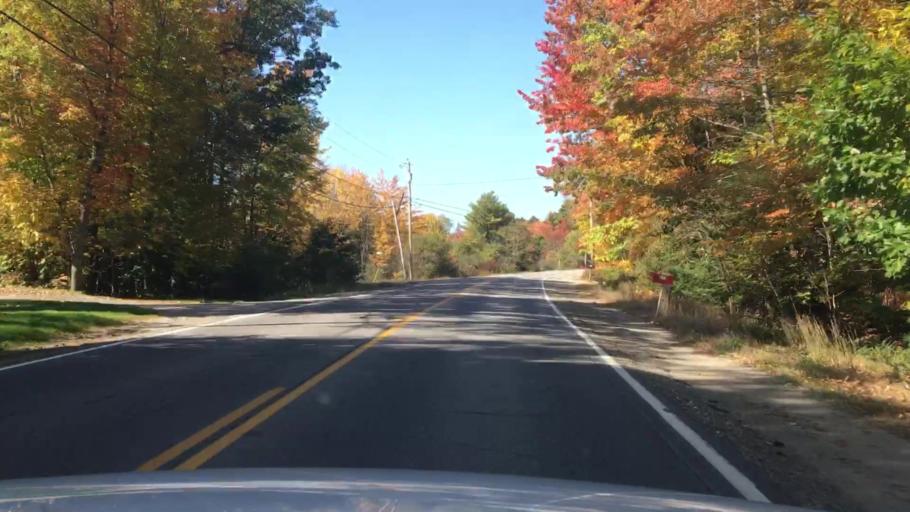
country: US
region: Maine
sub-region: Androscoggin County
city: Lisbon Falls
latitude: 44.0372
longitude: -69.9814
